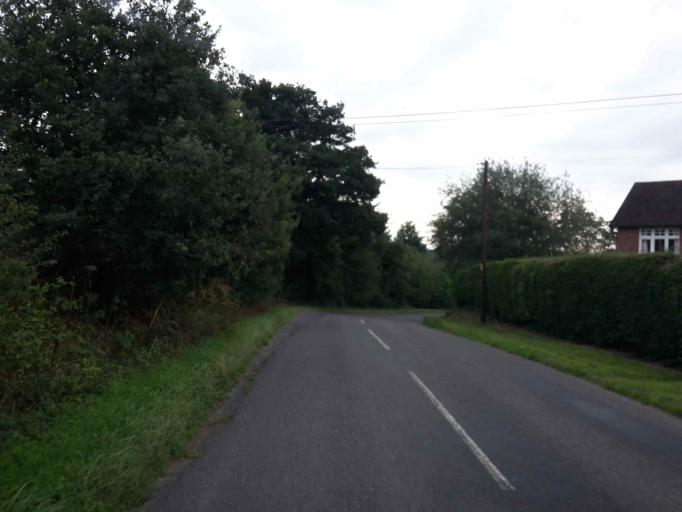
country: GB
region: England
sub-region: West Sussex
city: Rudgwick
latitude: 51.0744
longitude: -0.4522
